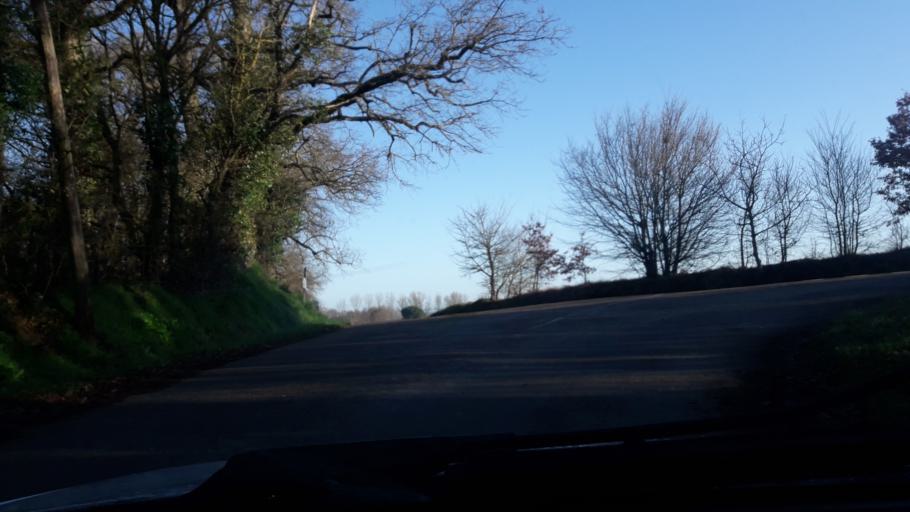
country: FR
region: Midi-Pyrenees
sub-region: Departement du Gers
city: Gimont
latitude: 43.6599
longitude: 0.9645
